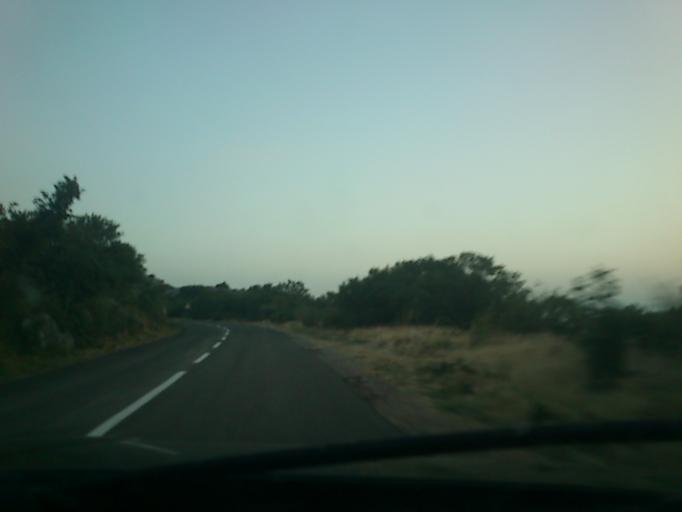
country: HR
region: Licko-Senjska
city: Senj
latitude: 44.9211
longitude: 14.9188
